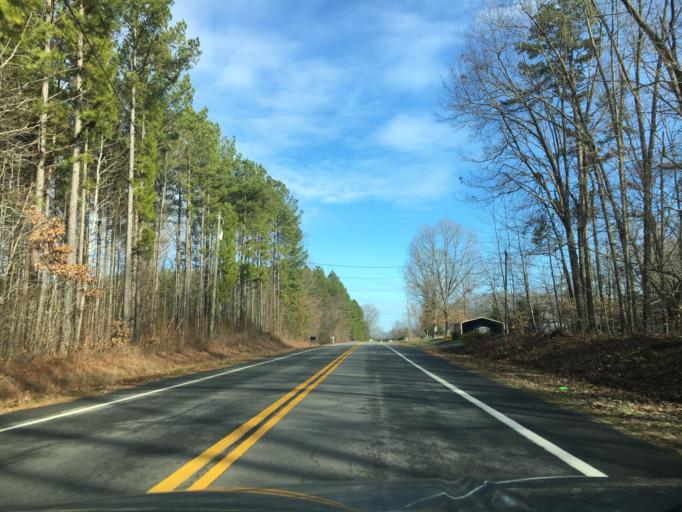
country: US
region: Virginia
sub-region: Halifax County
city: South Boston
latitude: 36.7351
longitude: -78.8578
